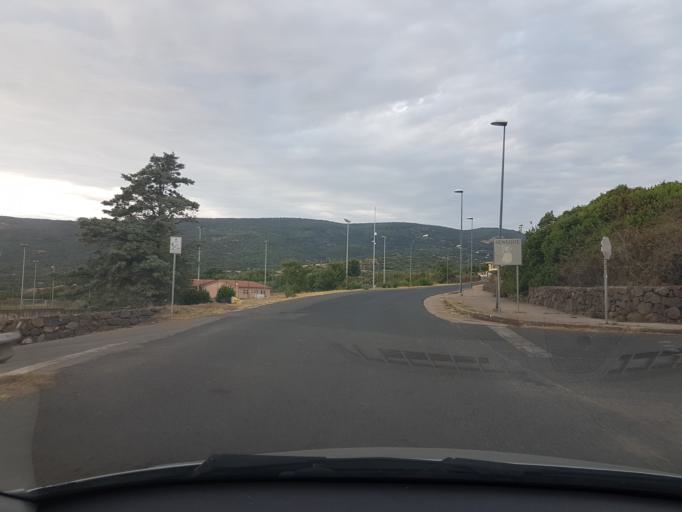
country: IT
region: Sardinia
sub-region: Provincia di Oristano
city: Seneghe
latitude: 40.0790
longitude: 8.6067
